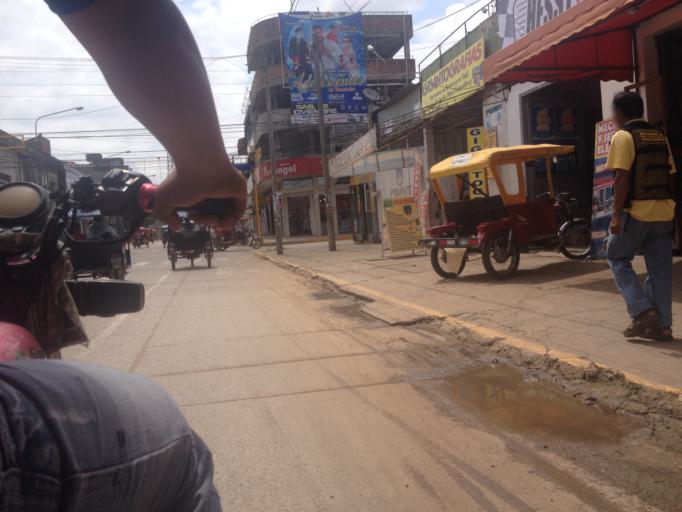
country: PE
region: Ucayali
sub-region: Provincia de Coronel Portillo
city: Pucallpa
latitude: -8.3799
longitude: -74.5361
